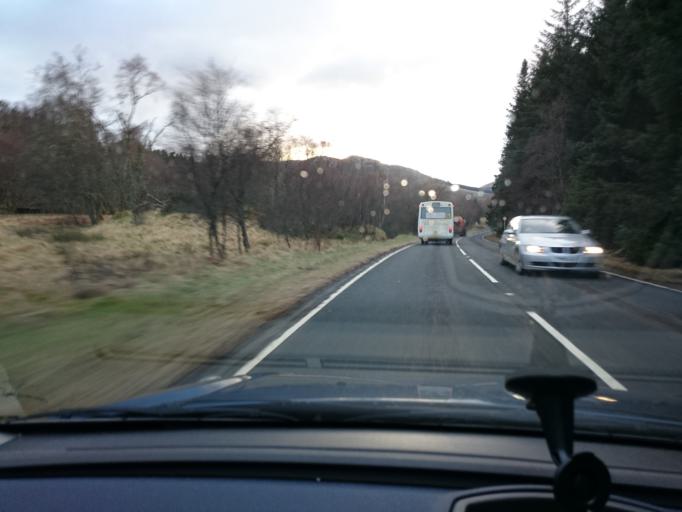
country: GB
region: Scotland
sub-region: Stirling
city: Callander
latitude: 56.3576
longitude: -4.3170
